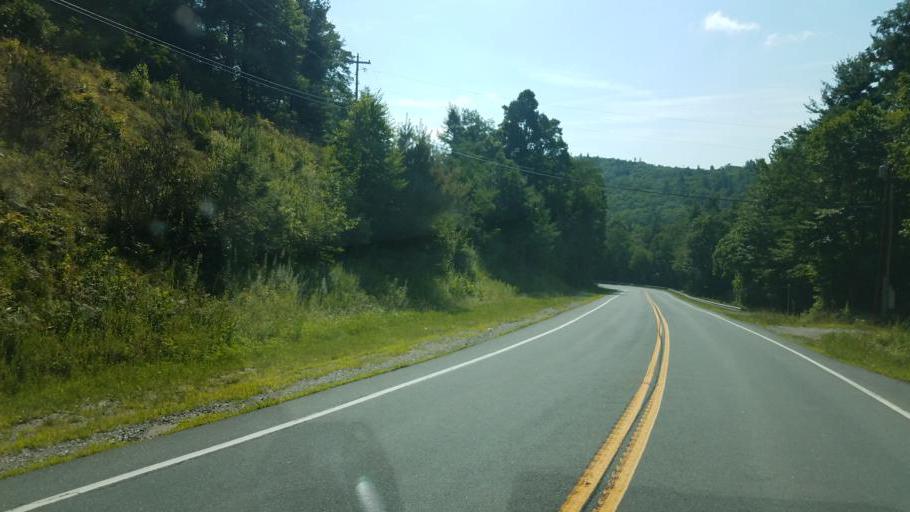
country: US
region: North Carolina
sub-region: Avery County
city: Newland
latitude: 35.9543
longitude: -81.8841
